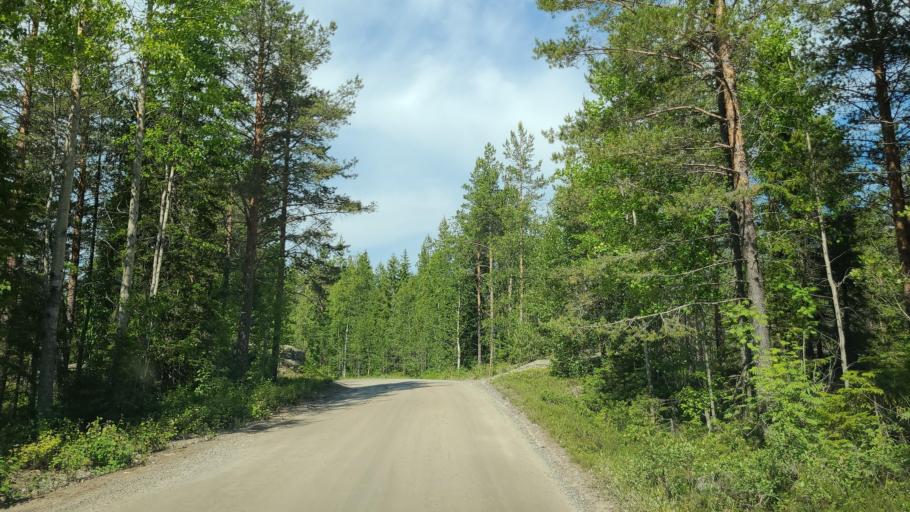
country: SE
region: Vaesterbotten
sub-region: Robertsfors Kommun
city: Robertsfors
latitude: 64.1567
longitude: 20.9427
